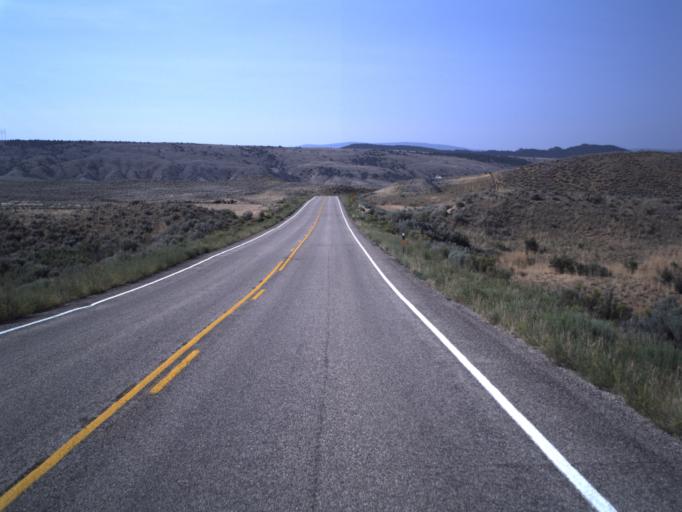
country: US
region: Utah
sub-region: Daggett County
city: Manila
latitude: 40.9902
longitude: -109.4366
